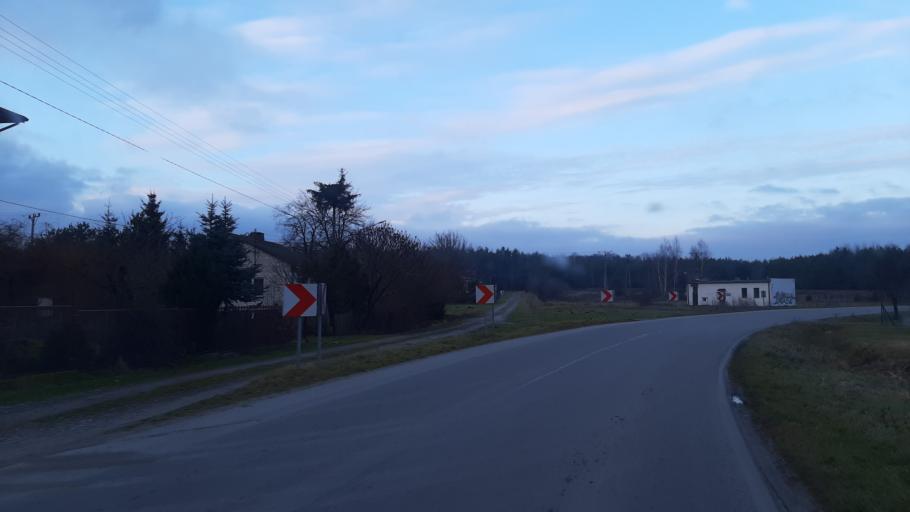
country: PL
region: Lublin Voivodeship
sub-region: Powiat lubelski
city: Garbow
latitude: 51.3942
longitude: 22.4091
